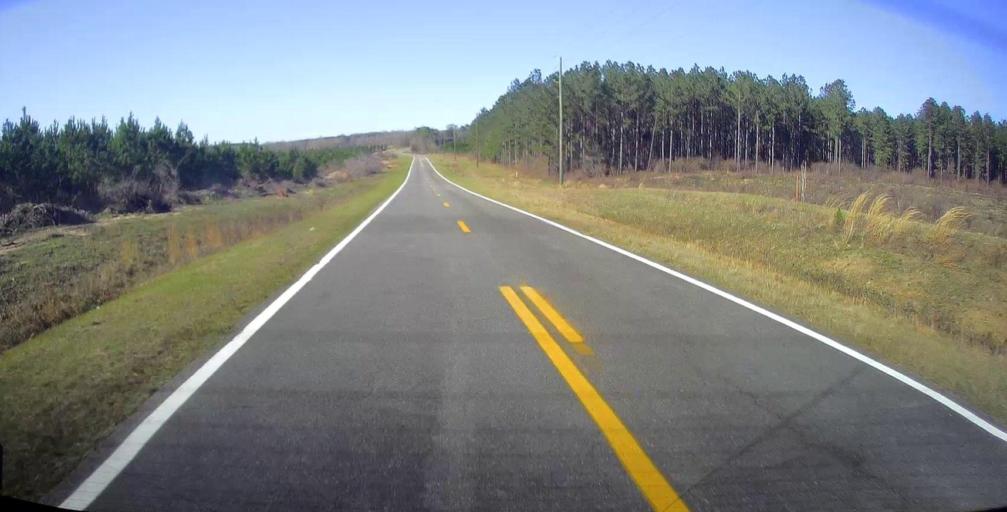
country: US
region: Georgia
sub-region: Taylor County
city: Reynolds
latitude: 32.5602
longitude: -84.0012
